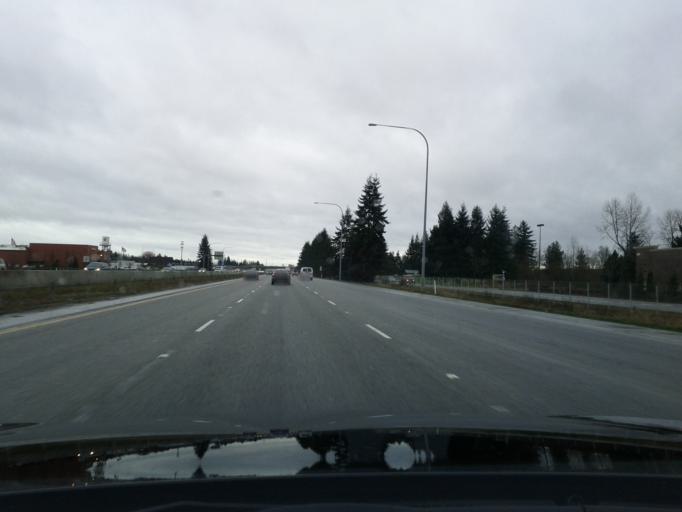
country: US
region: Washington
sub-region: Snohomish County
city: Smokey Point
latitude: 48.1464
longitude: -122.1879
